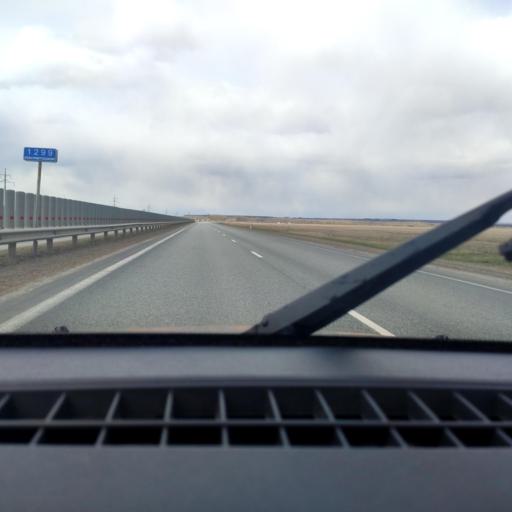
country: RU
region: Bashkortostan
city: Asanovo
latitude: 54.9948
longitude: 55.5073
